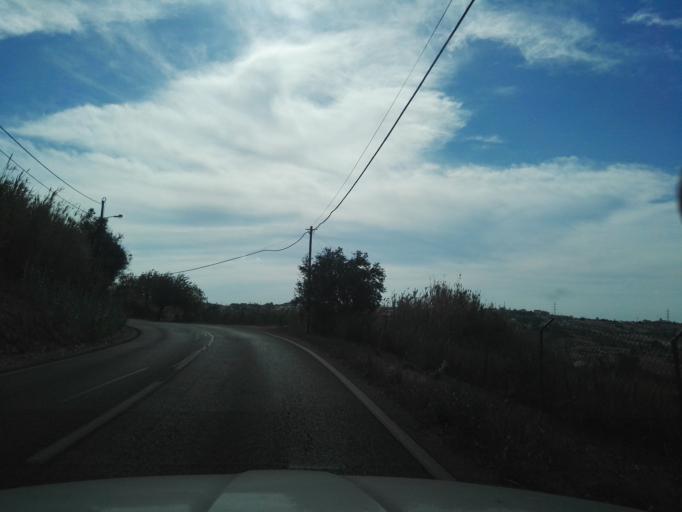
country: PT
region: Lisbon
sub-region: Vila Franca de Xira
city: Sao Joao dos Montes
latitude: 38.9606
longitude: -9.0317
